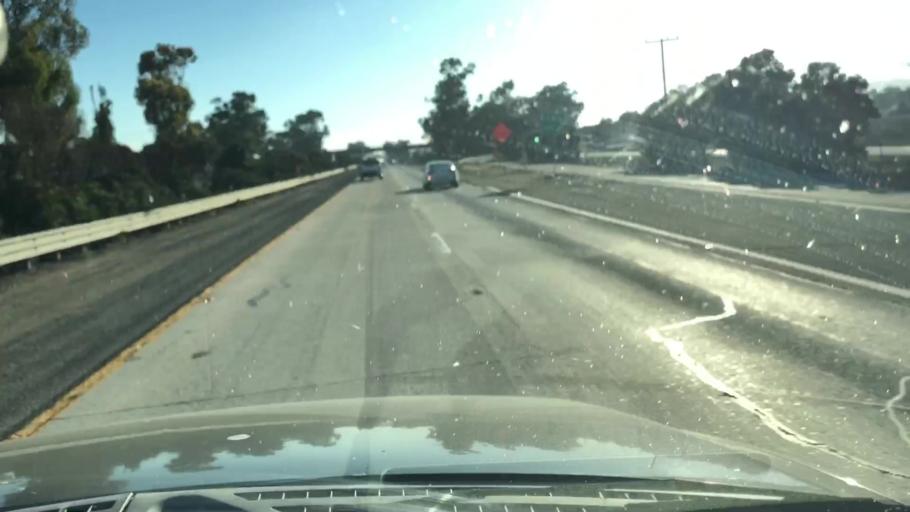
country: US
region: California
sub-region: Ventura County
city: Santa Paula
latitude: 34.3243
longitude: -119.0980
